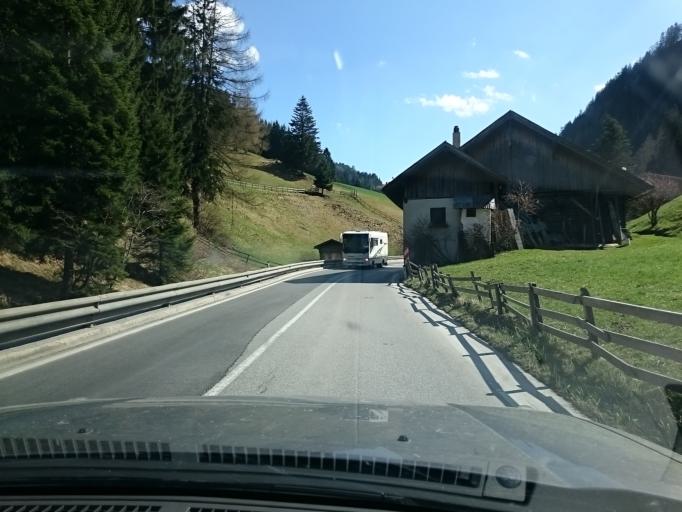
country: AT
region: Tyrol
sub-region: Politischer Bezirk Innsbruck Land
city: Gries am Brenner
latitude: 47.0573
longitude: 11.4855
